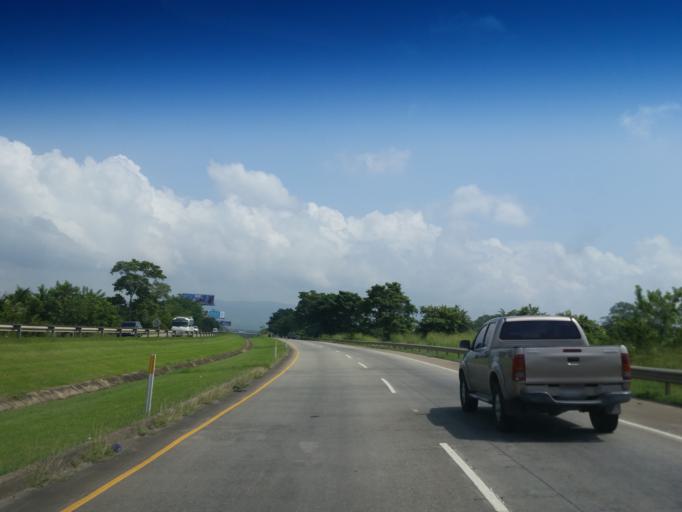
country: PA
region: Panama
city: Tocumen
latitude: 9.0466
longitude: -79.4010
